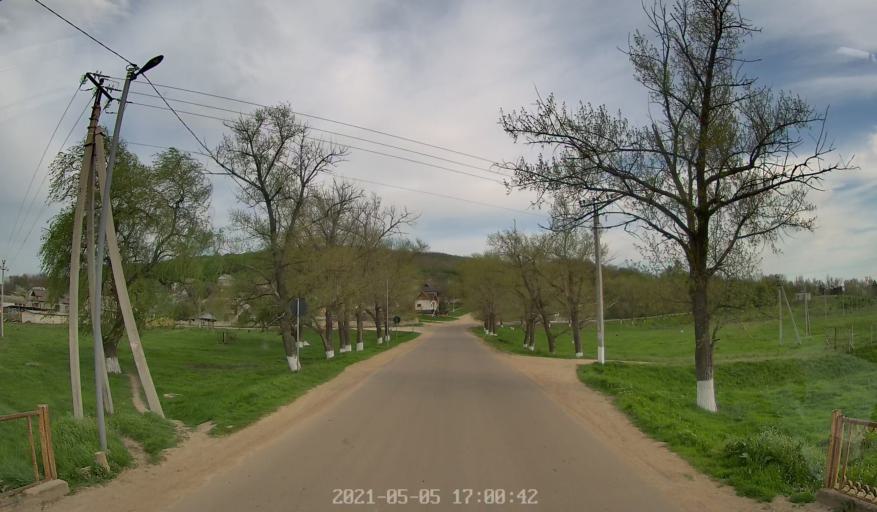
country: MD
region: Chisinau
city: Vadul lui Voda
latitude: 47.0631
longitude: 29.1322
